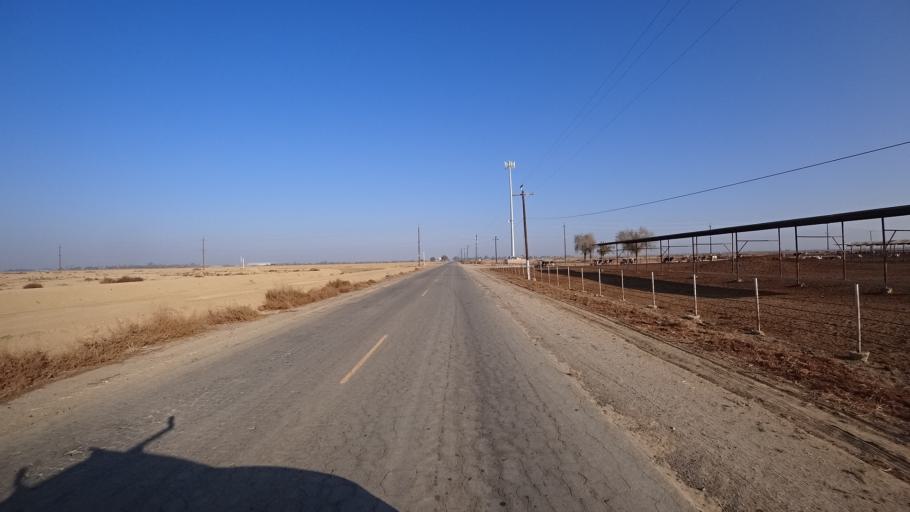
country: US
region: California
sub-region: Kern County
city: Weedpatch
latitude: 35.2215
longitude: -118.9677
